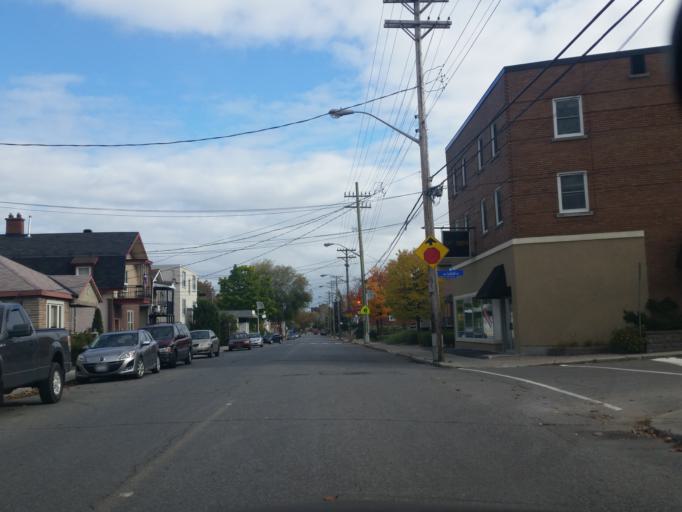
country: CA
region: Ontario
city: Ottawa
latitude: 45.4416
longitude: -75.6706
